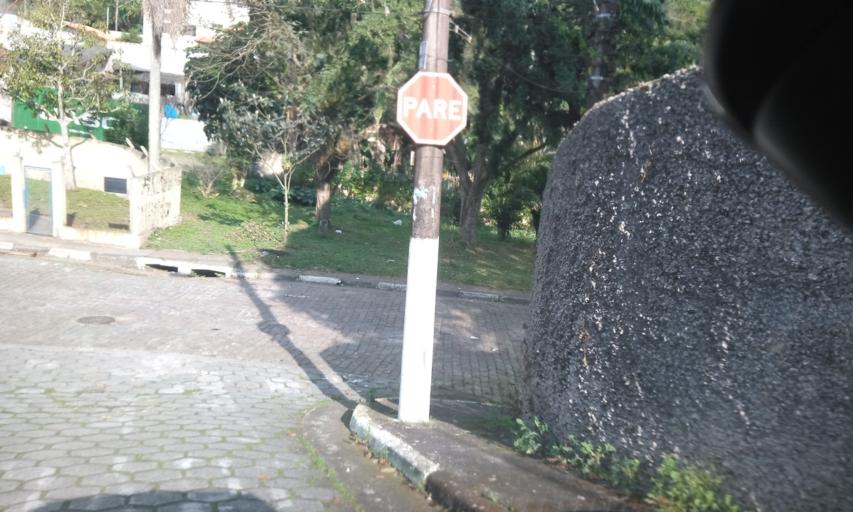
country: BR
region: Sao Paulo
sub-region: Sao Bernardo Do Campo
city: Sao Bernardo do Campo
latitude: -23.7806
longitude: -46.5330
